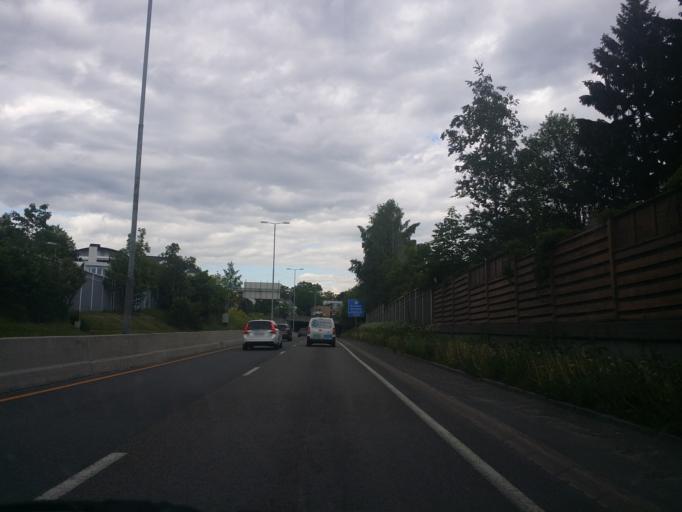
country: NO
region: Oslo
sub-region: Oslo
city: Sjolyststranda
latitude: 59.9419
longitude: 10.6959
